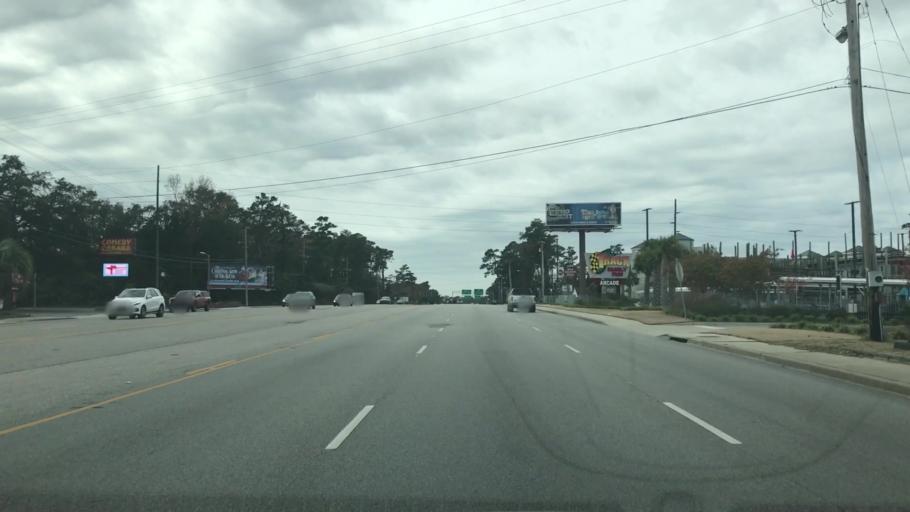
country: US
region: South Carolina
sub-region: Horry County
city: North Myrtle Beach
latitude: 33.7765
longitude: -78.7953
